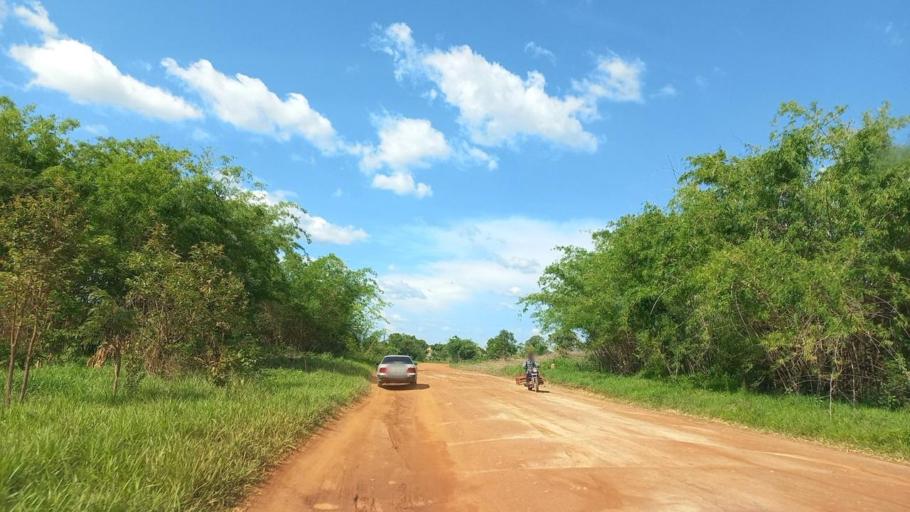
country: ZM
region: Copperbelt
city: Kitwe
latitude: -12.8588
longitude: 28.3844
